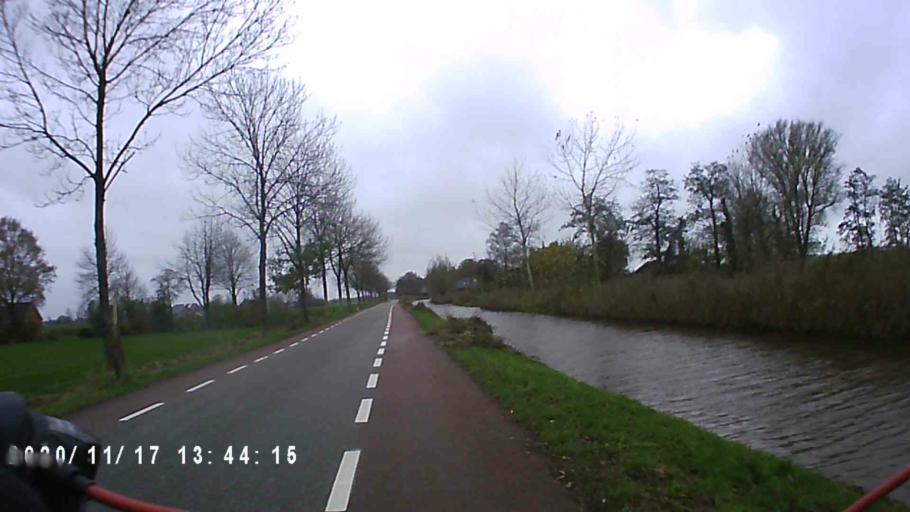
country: NL
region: Groningen
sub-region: Gemeente Zuidhorn
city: Zuidhorn
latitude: 53.2391
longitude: 6.3775
